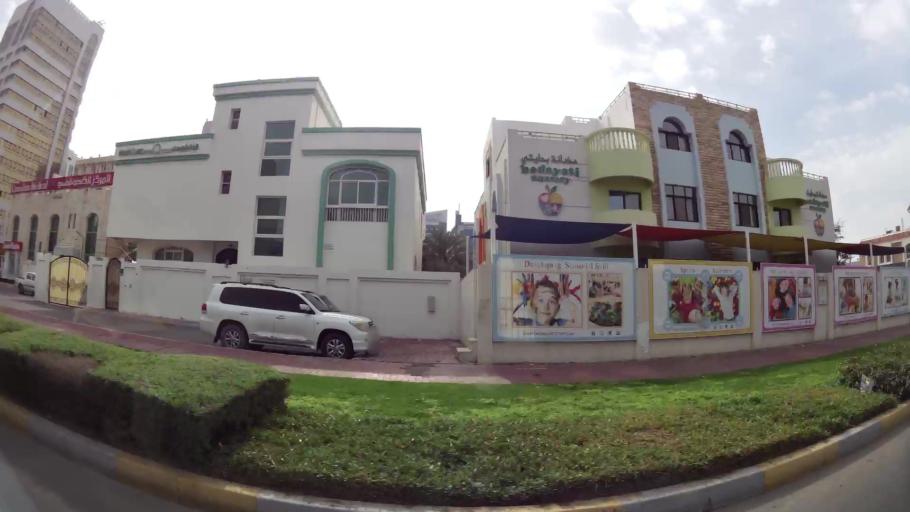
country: AE
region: Abu Dhabi
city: Abu Dhabi
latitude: 24.4619
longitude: 54.3766
